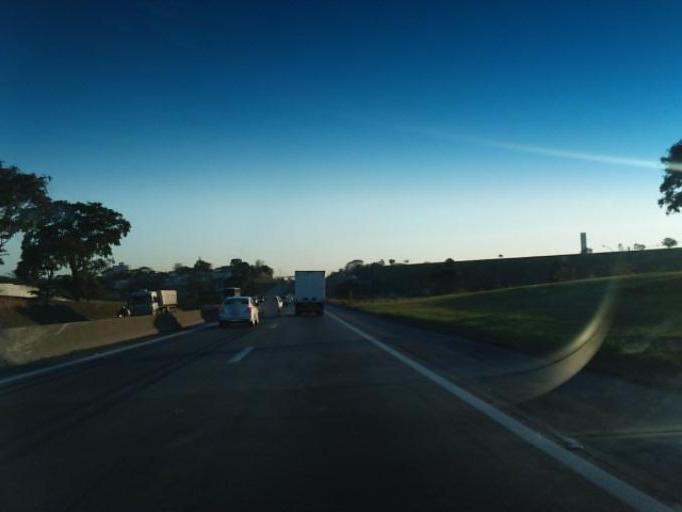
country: BR
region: Sao Paulo
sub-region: Sao Jose Dos Campos
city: Sao Jose dos Campos
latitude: -23.1628
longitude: -45.8068
